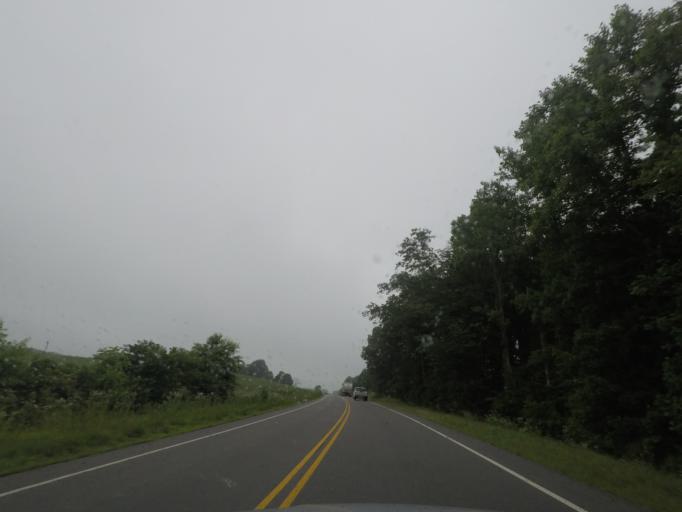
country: US
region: Virginia
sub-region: Prince Edward County
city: Farmville
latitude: 37.4367
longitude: -78.4522
